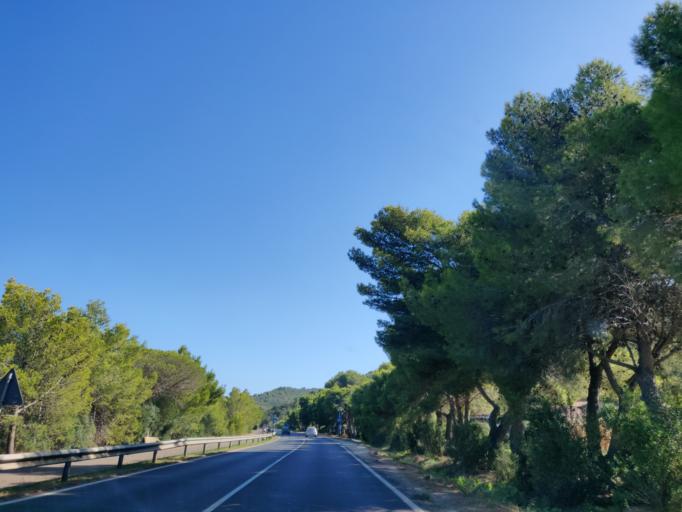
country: IT
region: Tuscany
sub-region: Provincia di Grosseto
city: Porto Ercole
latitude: 42.4203
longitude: 11.2029
